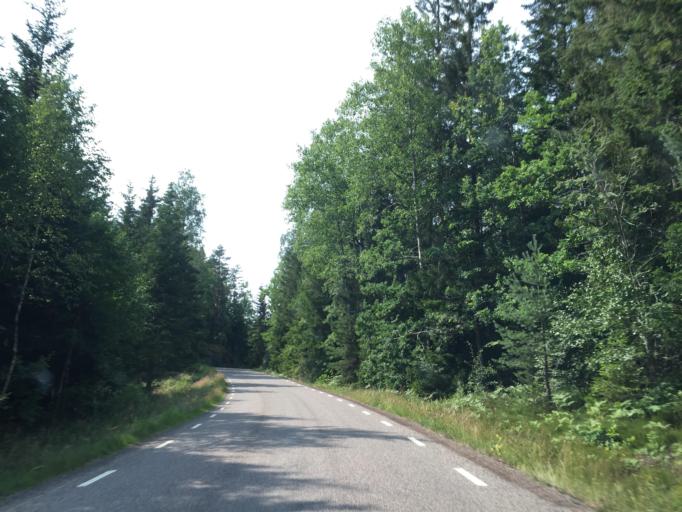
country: SE
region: Vaestra Goetaland
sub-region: Trollhattan
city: Sjuntorp
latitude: 58.3104
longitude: 12.1221
